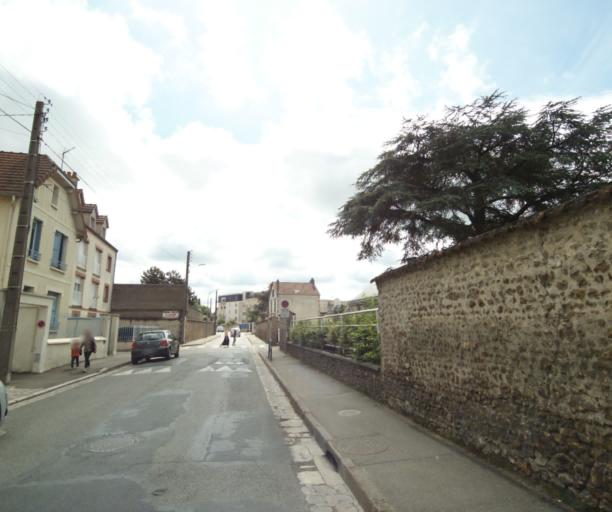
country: FR
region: Centre
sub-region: Departement d'Eure-et-Loir
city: Luisant
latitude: 48.4410
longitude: 1.4783
